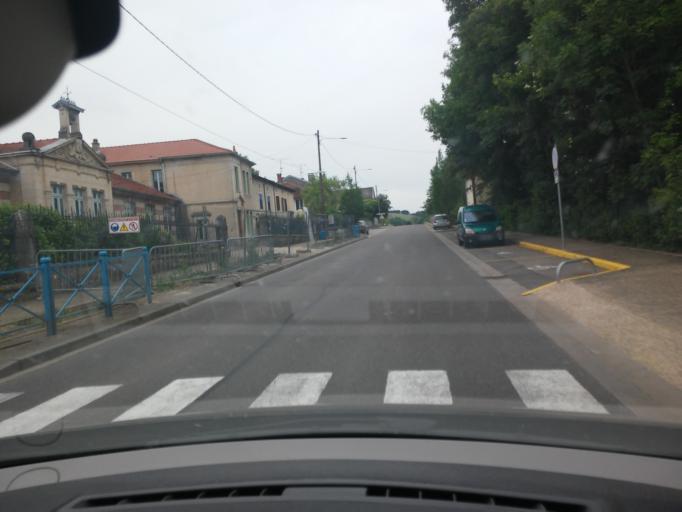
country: FR
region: Lorraine
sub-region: Departement de la Meuse
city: Lerouville
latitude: 48.8267
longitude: 5.5098
